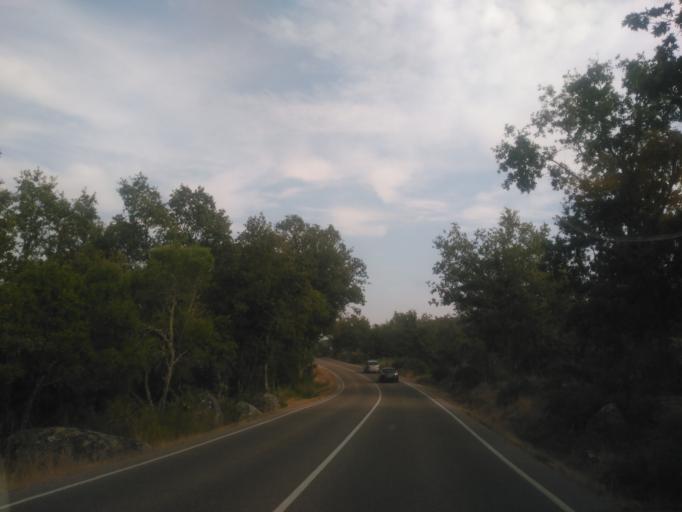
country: ES
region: Castille and Leon
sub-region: Provincia de Zamora
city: Galende
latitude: 42.1130
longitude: -6.6816
